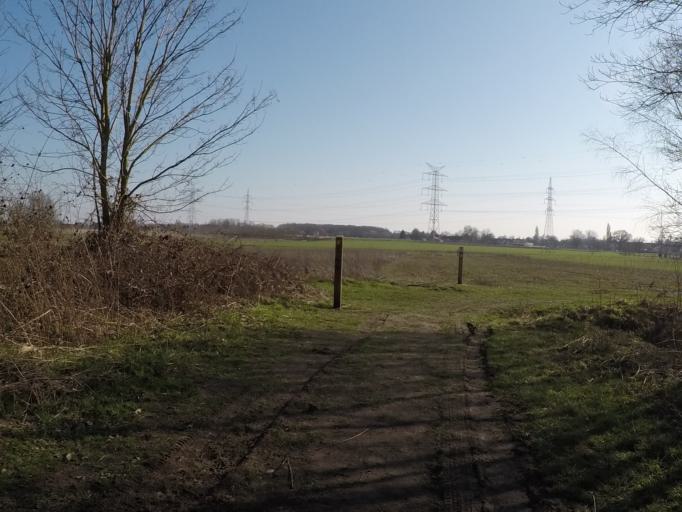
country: BE
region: Flanders
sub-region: Provincie Antwerpen
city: Aartselaar
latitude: 51.1196
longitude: 4.3781
